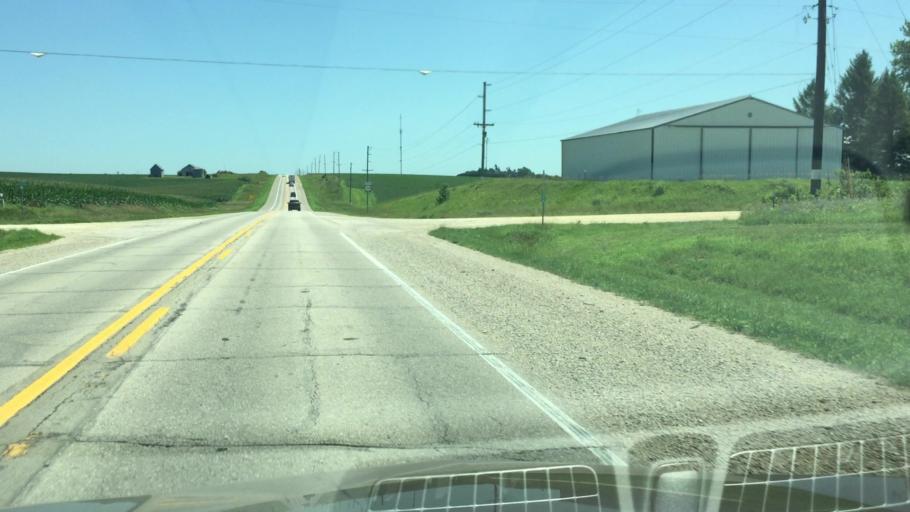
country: US
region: Iowa
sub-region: Cedar County
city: Mechanicsville
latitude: 41.8886
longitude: -91.1913
